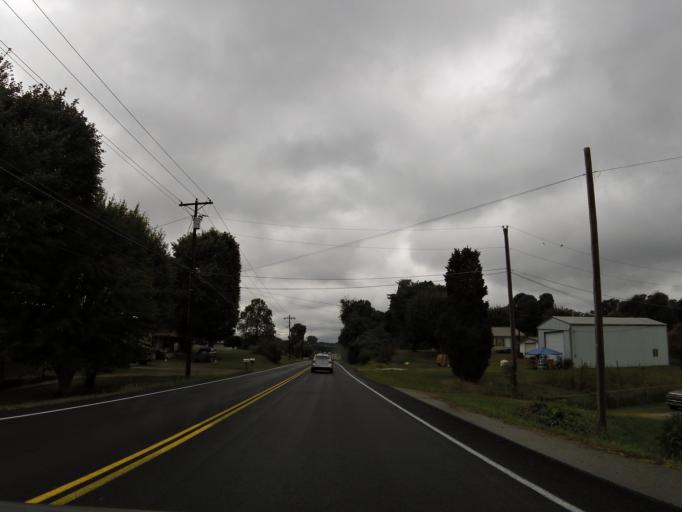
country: US
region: Tennessee
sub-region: Loudon County
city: Loudon
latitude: 35.7726
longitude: -84.3077
